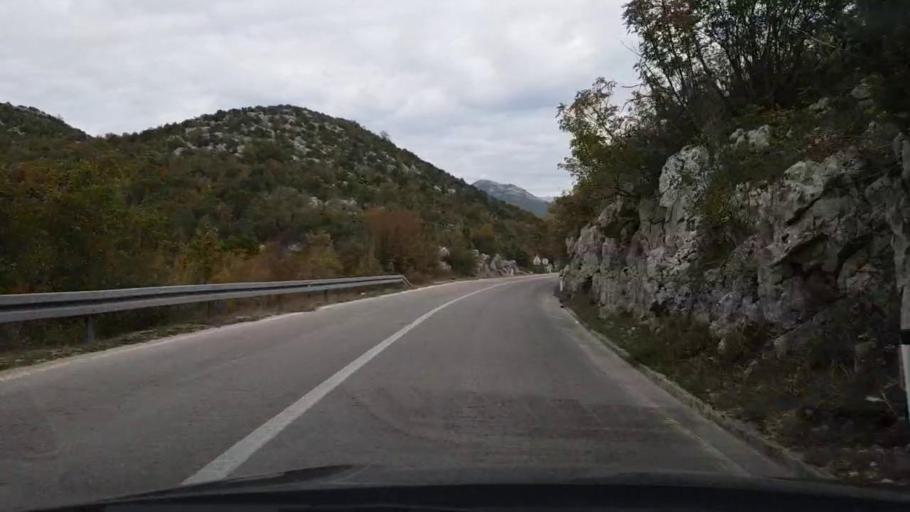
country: HR
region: Dubrovacko-Neretvanska
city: Cibaca
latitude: 42.6700
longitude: 18.2236
